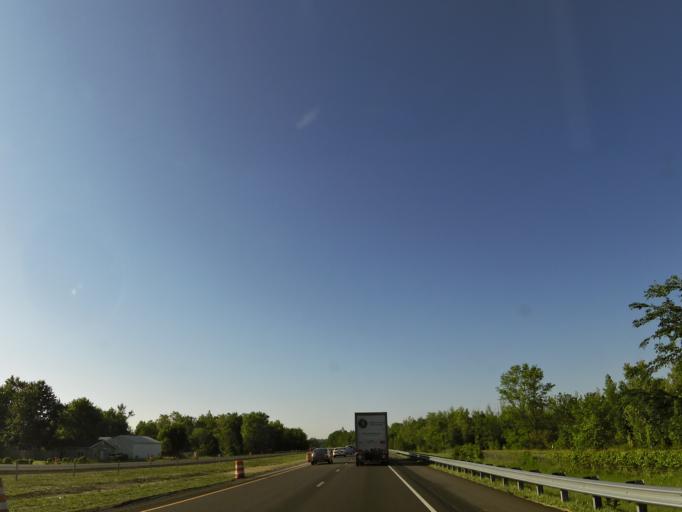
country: US
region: Indiana
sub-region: Jackson County
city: Seymour
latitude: 38.9197
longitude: -85.8360
